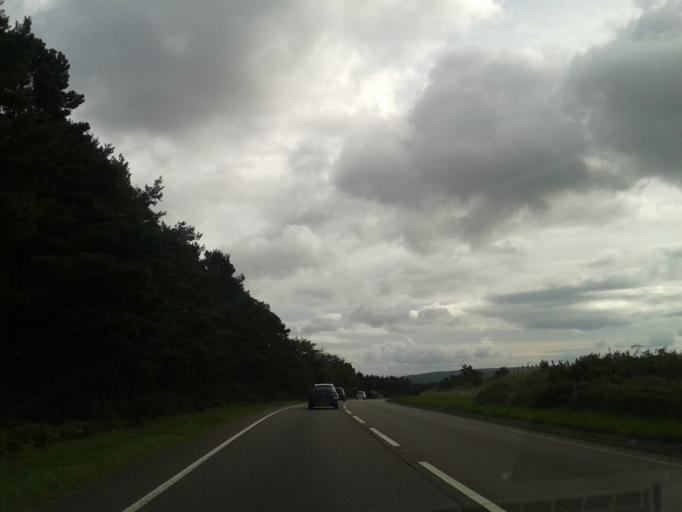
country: GB
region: Scotland
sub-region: Moray
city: Lhanbryd
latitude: 57.6309
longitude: -3.1754
